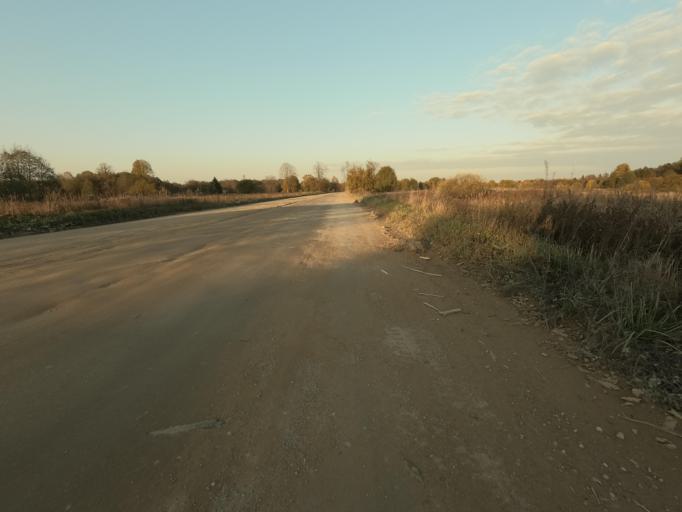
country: RU
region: Leningrad
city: Lyuban'
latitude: 59.0243
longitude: 31.1006
